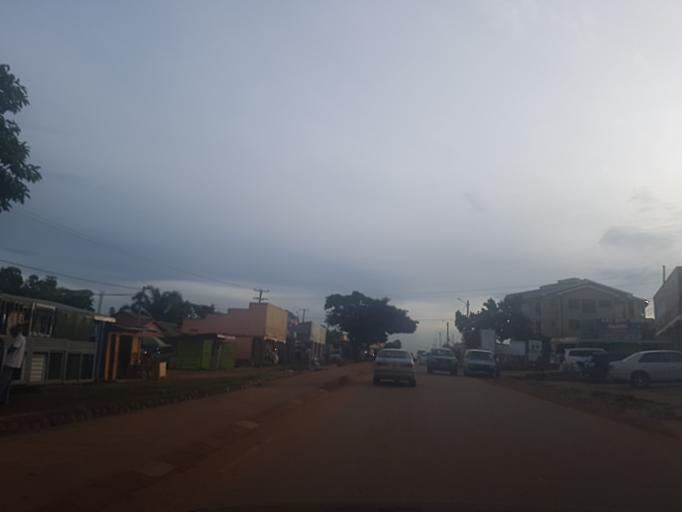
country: UG
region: Central Region
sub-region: Wakiso District
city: Bweyogerere
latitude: 0.3926
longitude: 32.6611
